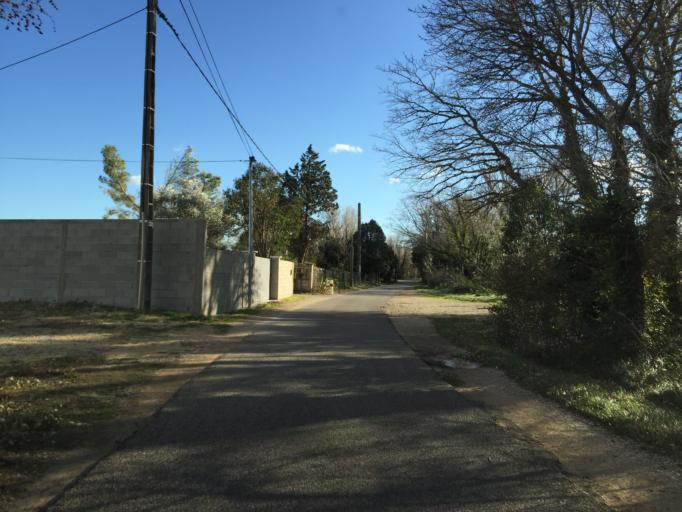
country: FR
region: Provence-Alpes-Cote d'Azur
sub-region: Departement du Vaucluse
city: Chateauneuf-du-Pape
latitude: 44.0275
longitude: 4.8431
